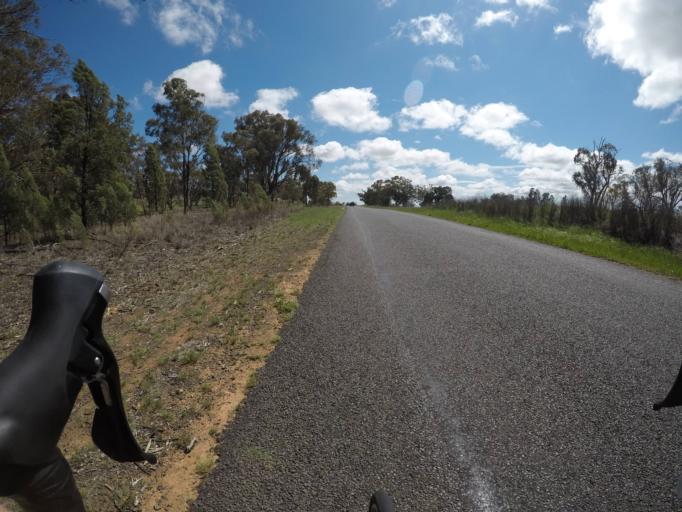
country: AU
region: New South Wales
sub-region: Dubbo Municipality
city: Dubbo
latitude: -32.5191
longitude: 148.5546
